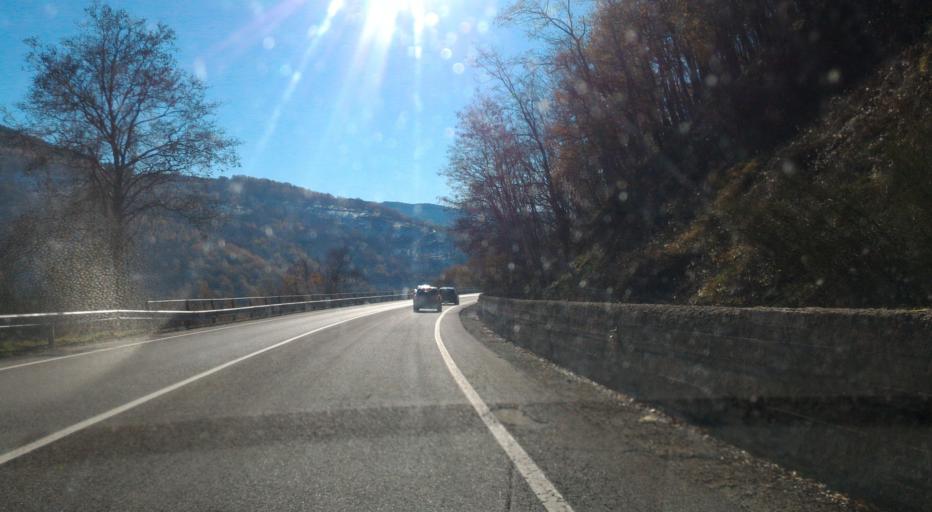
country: IT
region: Calabria
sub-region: Provincia di Cosenza
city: Spezzano della Sila
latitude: 39.3019
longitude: 16.3554
